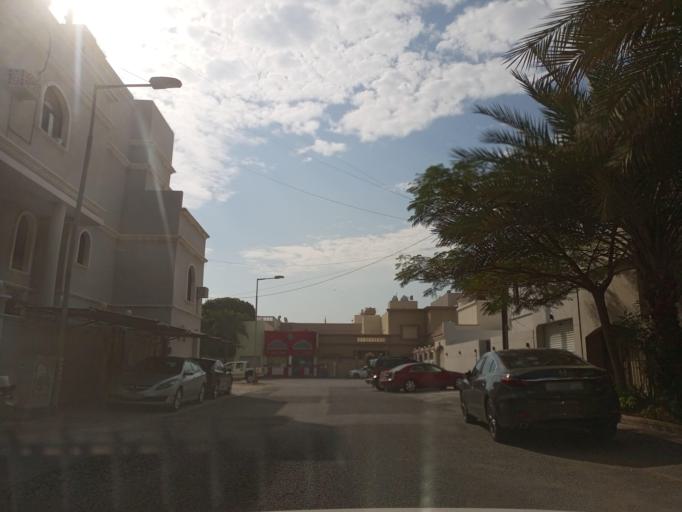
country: BH
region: Muharraq
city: Al Hadd
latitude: 26.2516
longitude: 50.6432
